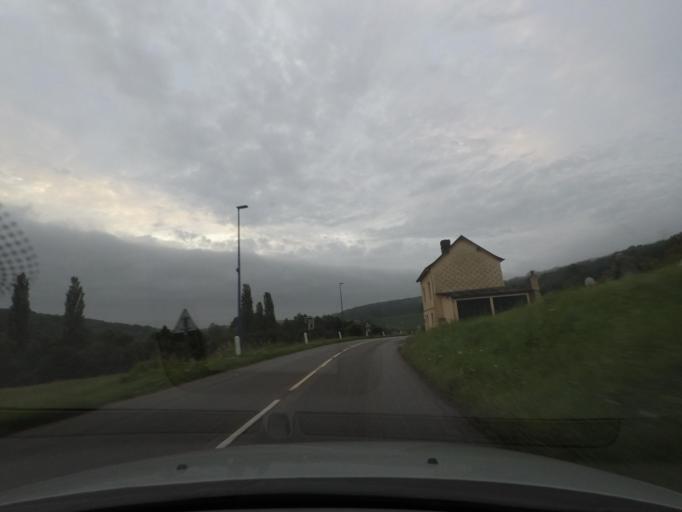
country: FR
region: Haute-Normandie
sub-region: Departement de la Seine-Maritime
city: Fontaine-le-Bourg
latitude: 49.5597
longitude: 1.1405
